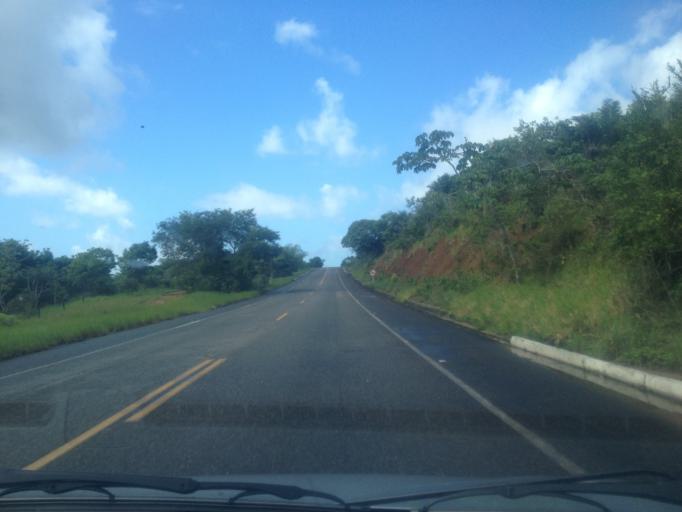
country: BR
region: Bahia
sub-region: Conde
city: Conde
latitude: -12.0539
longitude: -37.7358
